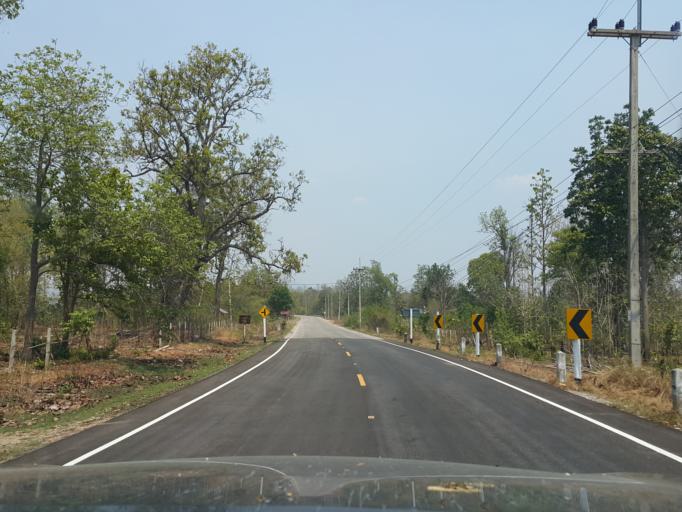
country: TH
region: Lampang
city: Mae Phrik
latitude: 17.5458
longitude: 99.1317
